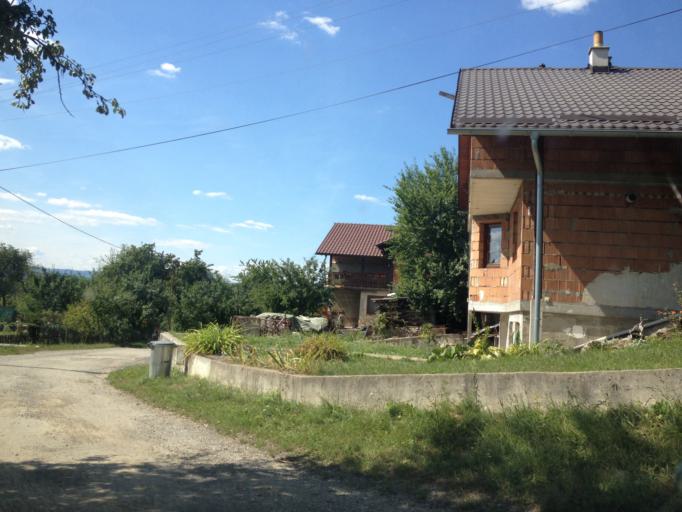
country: SK
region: Nitriansky
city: Puchov
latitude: 49.0579
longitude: 18.3480
